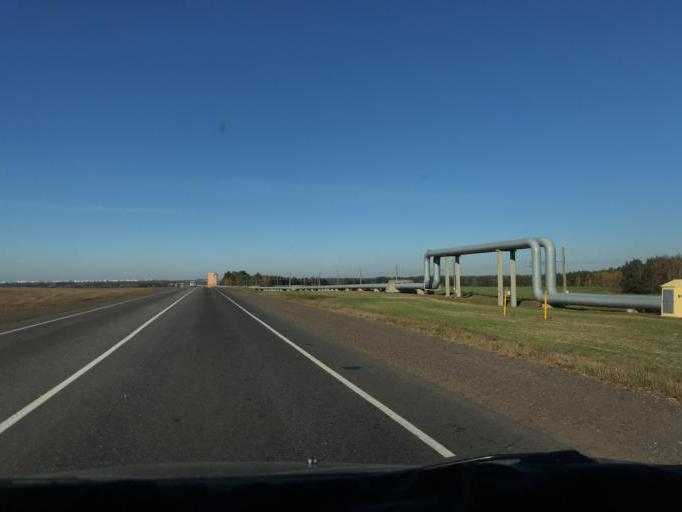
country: BY
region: Gomel
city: Mazyr
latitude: 51.9655
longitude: 29.2619
